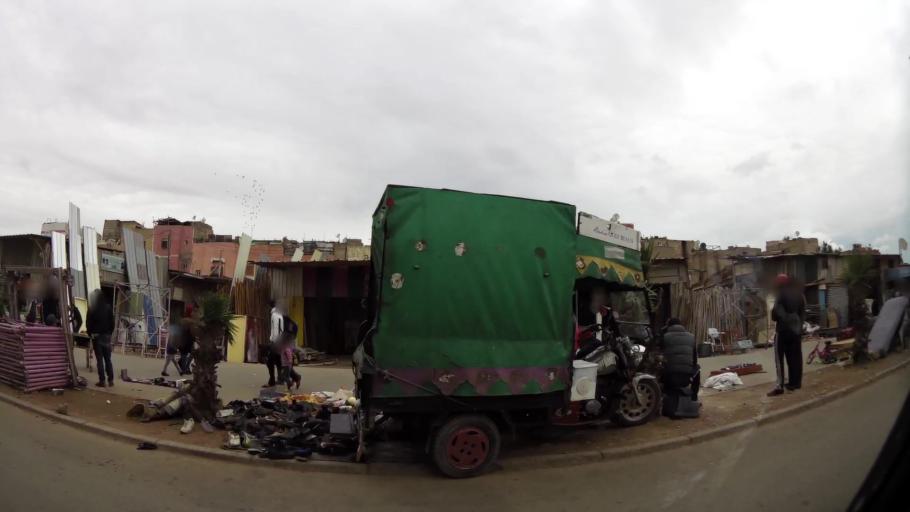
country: MA
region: Grand Casablanca
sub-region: Mediouna
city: Tit Mellil
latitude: 33.5603
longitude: -7.5439
